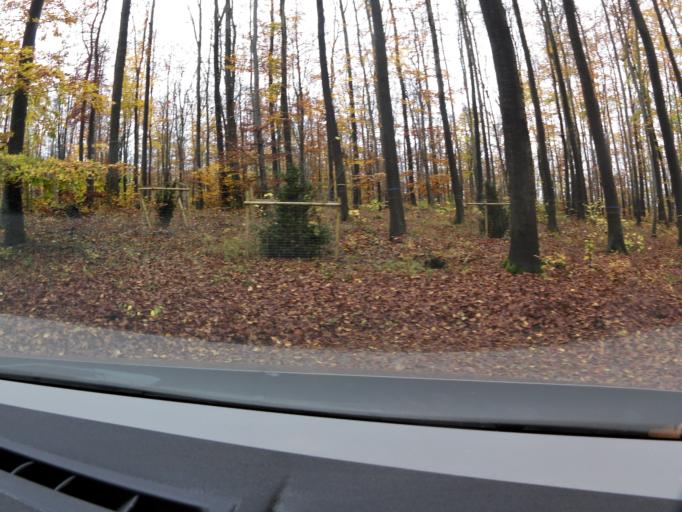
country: DE
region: Hesse
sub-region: Regierungsbezirk Kassel
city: Herleshausen
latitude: 51.0424
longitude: 10.1274
